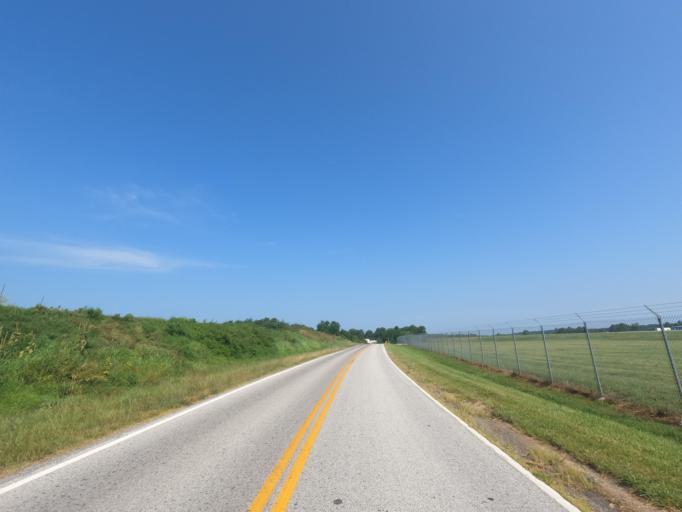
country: US
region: Maryland
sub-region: Carroll County
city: Westminster
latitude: 39.6030
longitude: -77.0064
